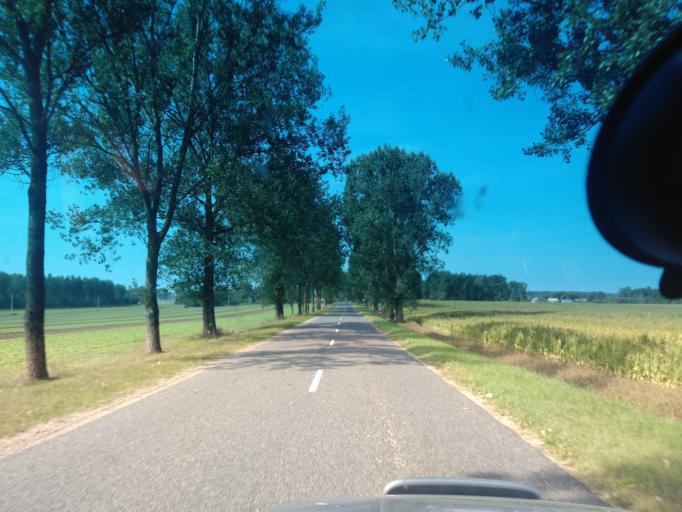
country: BY
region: Minsk
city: Kapyl'
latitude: 53.2715
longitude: 27.2170
